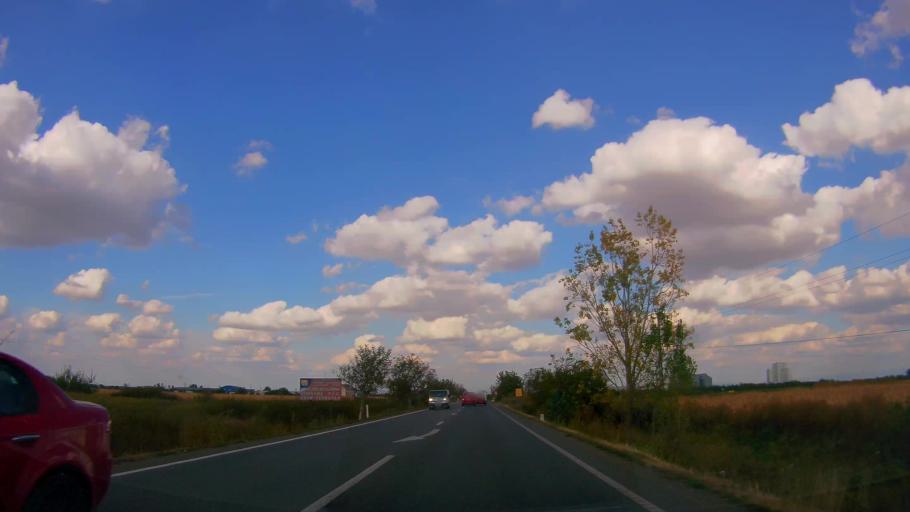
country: RO
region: Satu Mare
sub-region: Comuna Botiz
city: Botiz
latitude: 47.8172
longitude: 22.9320
